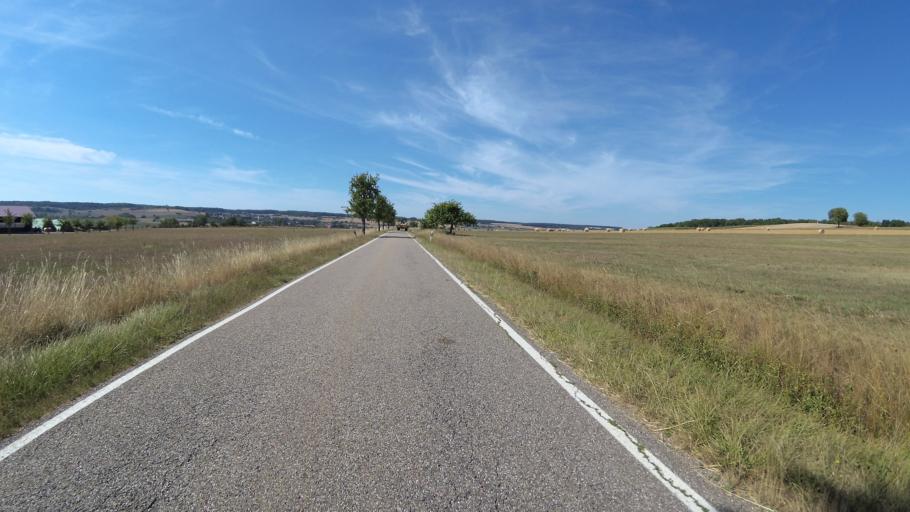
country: FR
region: Lorraine
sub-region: Departement de la Moselle
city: Petit-Rederching
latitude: 49.1332
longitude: 7.2947
